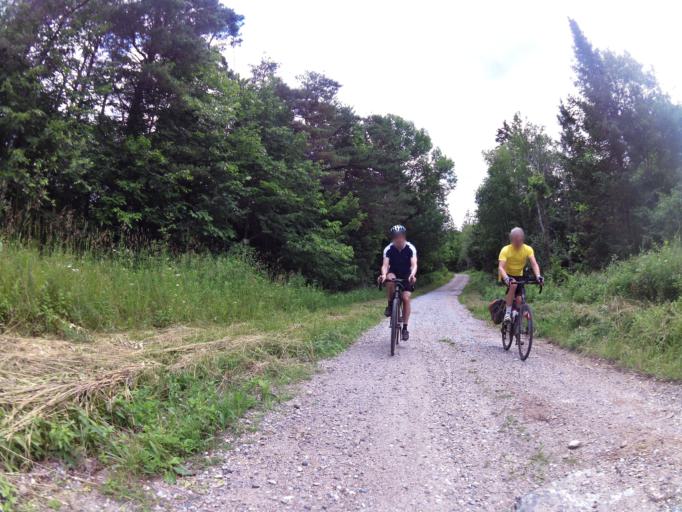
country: CA
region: Ontario
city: Perth
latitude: 45.0266
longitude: -76.5448
